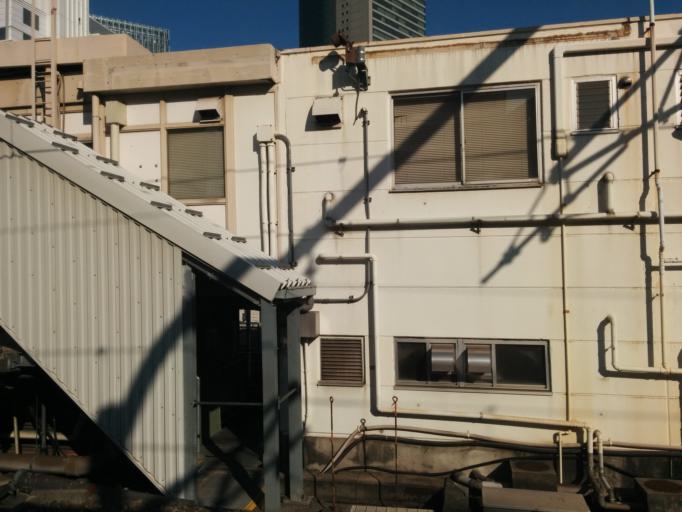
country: JP
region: Aichi
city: Nagoya-shi
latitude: 35.1687
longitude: 136.8821
